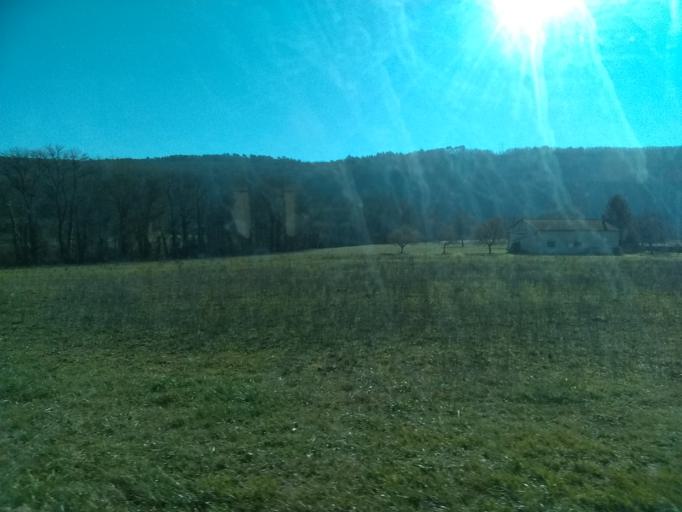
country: FR
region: Aquitaine
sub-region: Departement de la Dordogne
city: Montignac
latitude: 45.0804
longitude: 1.1867
